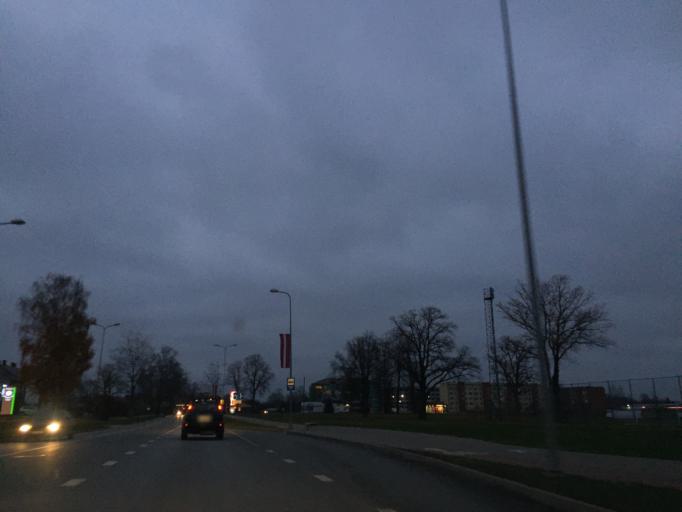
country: LV
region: Valmieras Rajons
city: Valmiera
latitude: 57.5293
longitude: 25.3878
